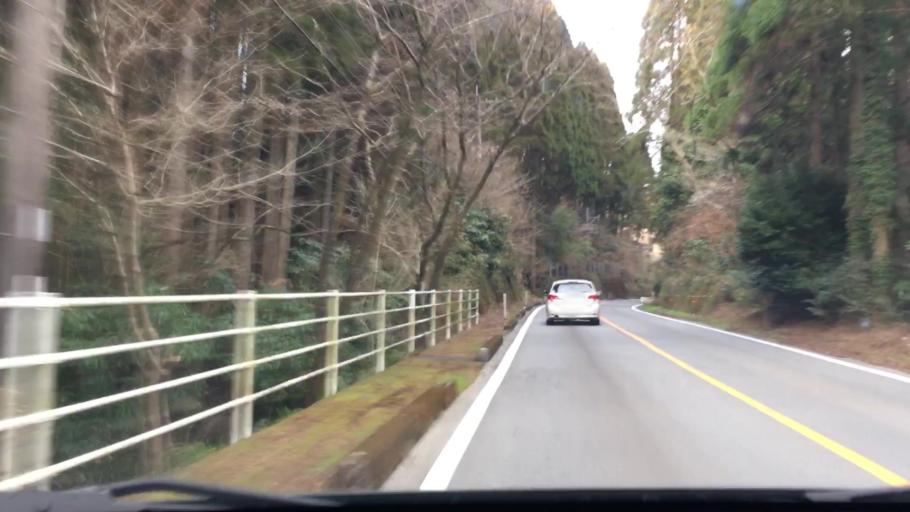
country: JP
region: Miyazaki
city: Nichinan
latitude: 31.7273
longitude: 131.3303
